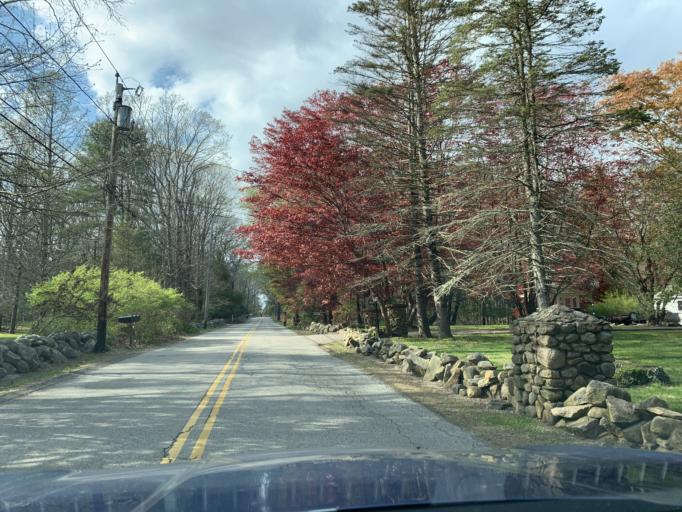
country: US
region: Rhode Island
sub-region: Washington County
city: Exeter
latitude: 41.5982
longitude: -71.5205
